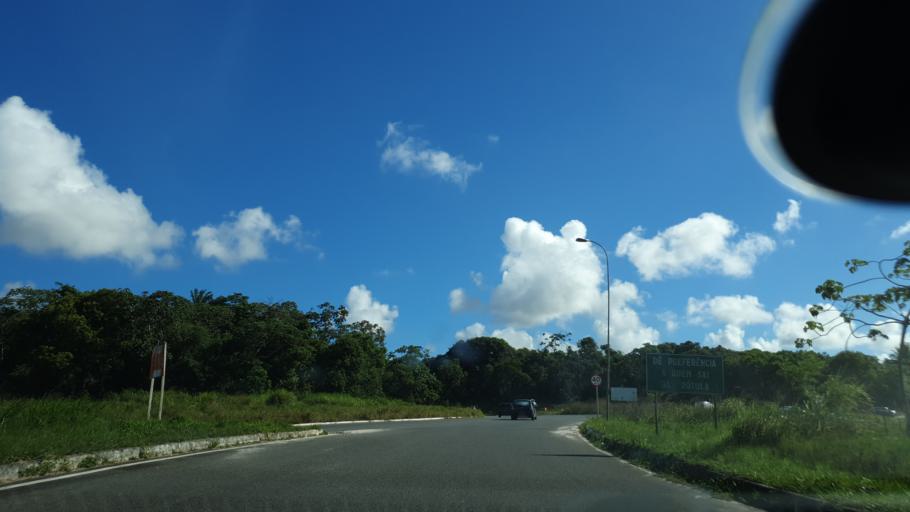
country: BR
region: Bahia
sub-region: Camacari
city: Camacari
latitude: -12.6792
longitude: -38.2833
